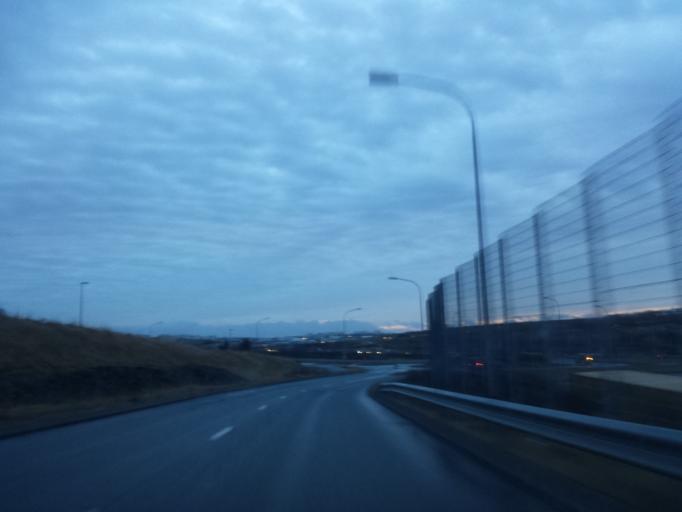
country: IS
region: Capital Region
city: Mosfellsbaer
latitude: 64.1395
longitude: -21.7526
